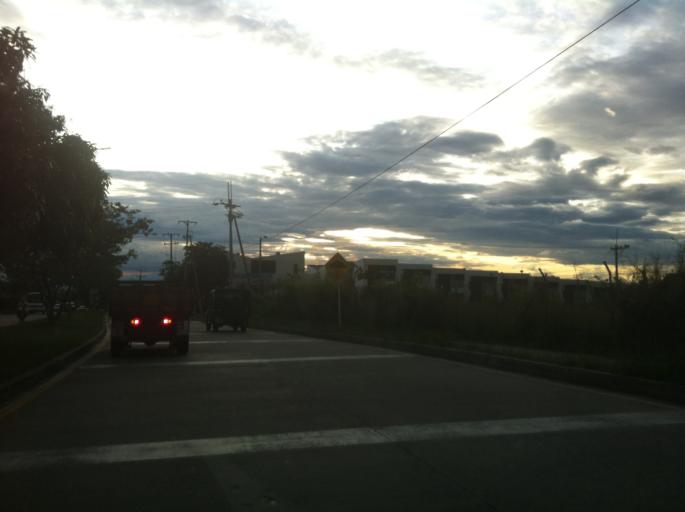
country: CO
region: Quindio
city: Calarca
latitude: 4.5660
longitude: -75.6533
